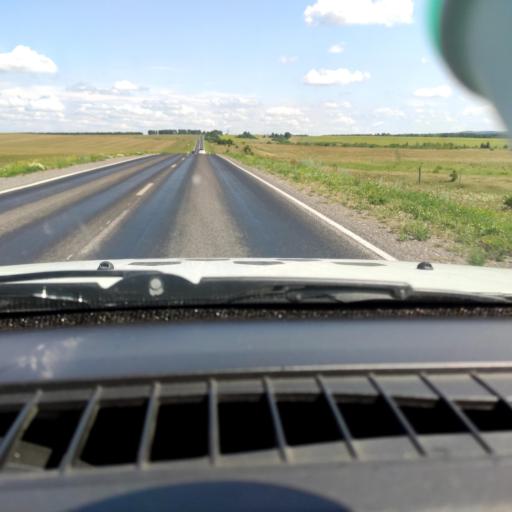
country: RU
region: Bashkortostan
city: Mesyagutovo
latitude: 55.4582
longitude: 58.4187
